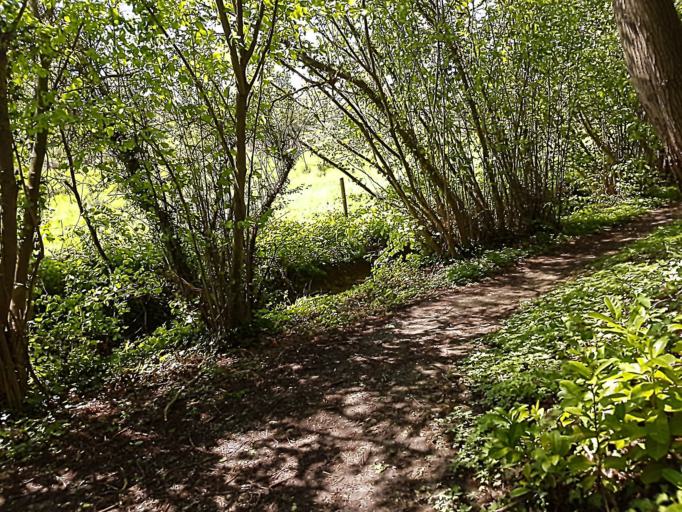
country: BE
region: Flanders
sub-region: Provincie Vlaams-Brabant
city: Tienen
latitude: 50.8404
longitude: 4.9181
